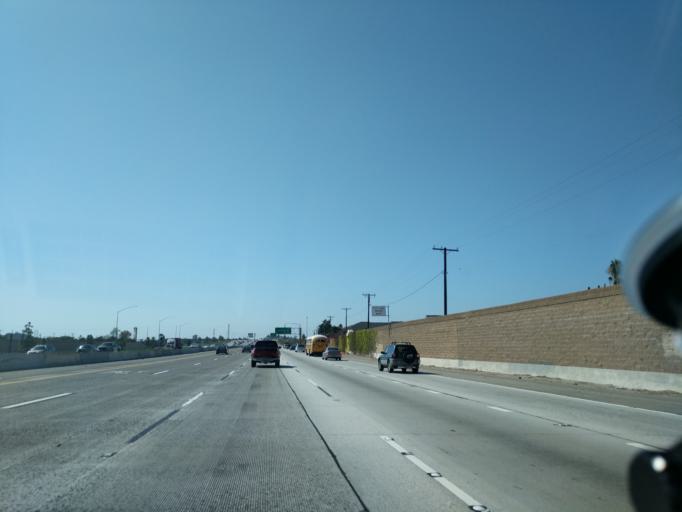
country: US
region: California
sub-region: Orange County
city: Westminster
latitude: 33.7708
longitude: -117.9851
